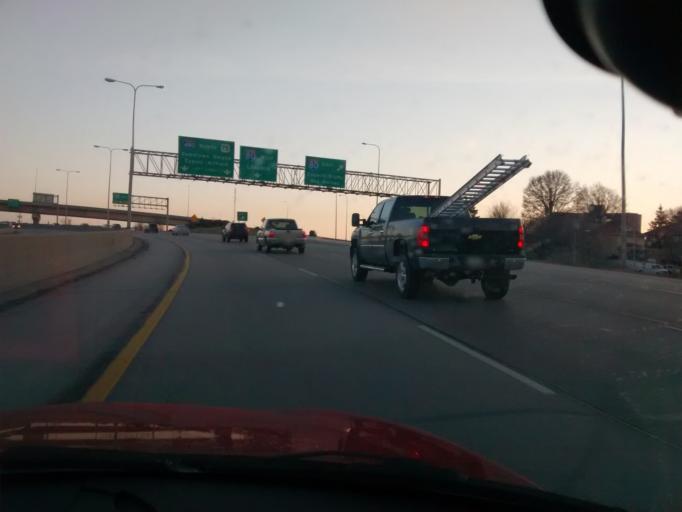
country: US
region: Nebraska
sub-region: Douglas County
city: Omaha
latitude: 41.2228
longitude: -95.9519
